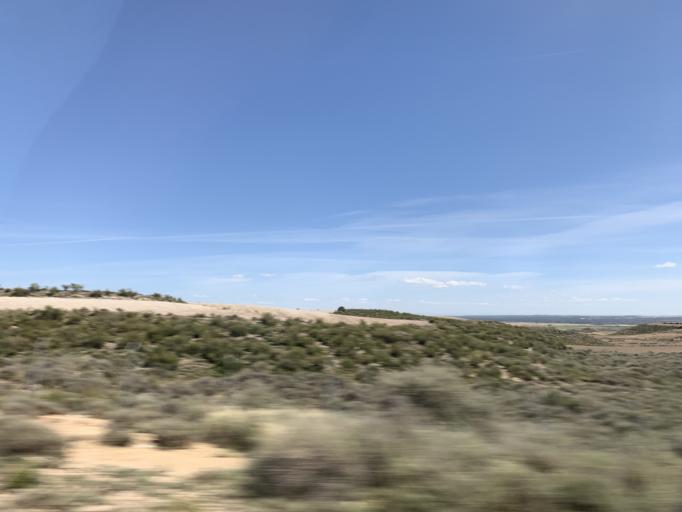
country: ES
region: Aragon
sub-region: Provincia de Huesca
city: Candasnos
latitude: 41.5272
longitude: 0.0272
